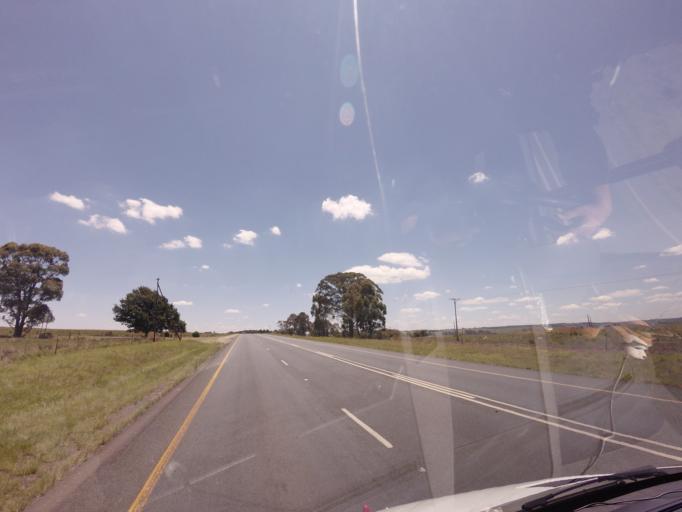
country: ZA
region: Mpumalanga
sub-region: Nkangala District Municipality
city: Belfast
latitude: -25.7335
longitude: 30.1190
